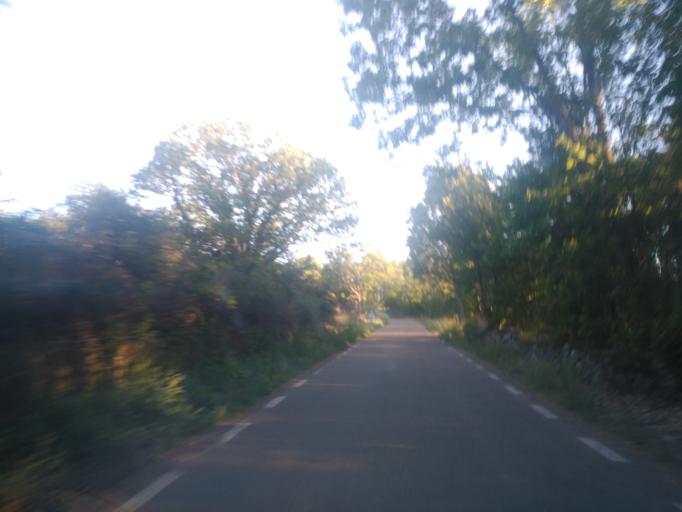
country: ES
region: Castille and Leon
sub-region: Provincia de Salamanca
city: Candelario
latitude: 40.3771
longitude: -5.7526
